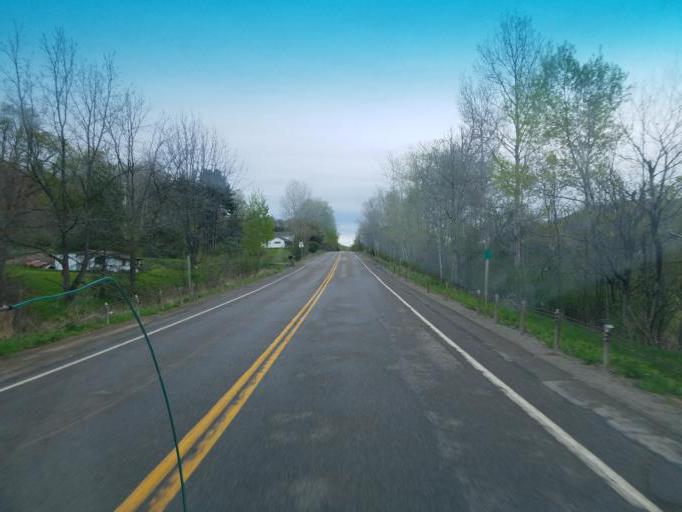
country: US
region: New York
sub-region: Allegany County
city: Wellsville
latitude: 42.0054
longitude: -77.8496
